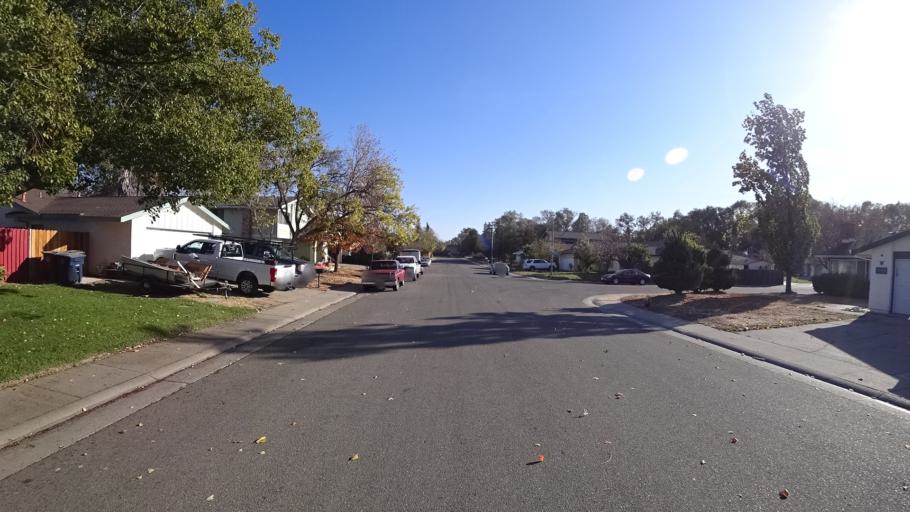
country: US
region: California
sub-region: Sacramento County
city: Antelope
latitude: 38.6979
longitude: -121.3135
